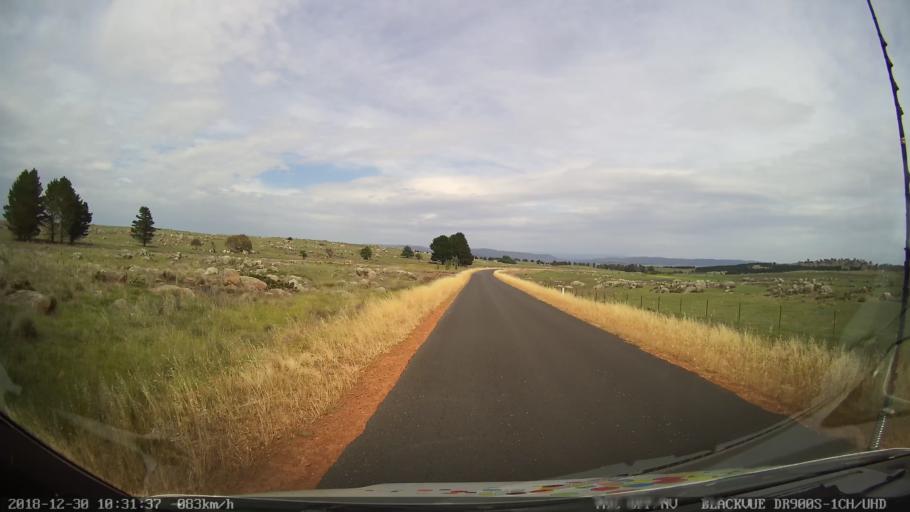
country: AU
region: New South Wales
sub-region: Snowy River
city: Berridale
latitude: -36.5046
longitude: 148.8774
